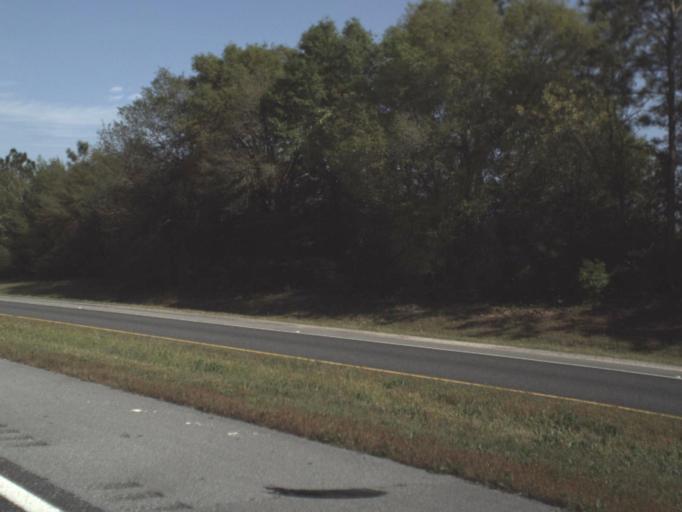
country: US
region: Florida
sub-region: Okaloosa County
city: Crestview
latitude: 30.7257
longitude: -86.5646
